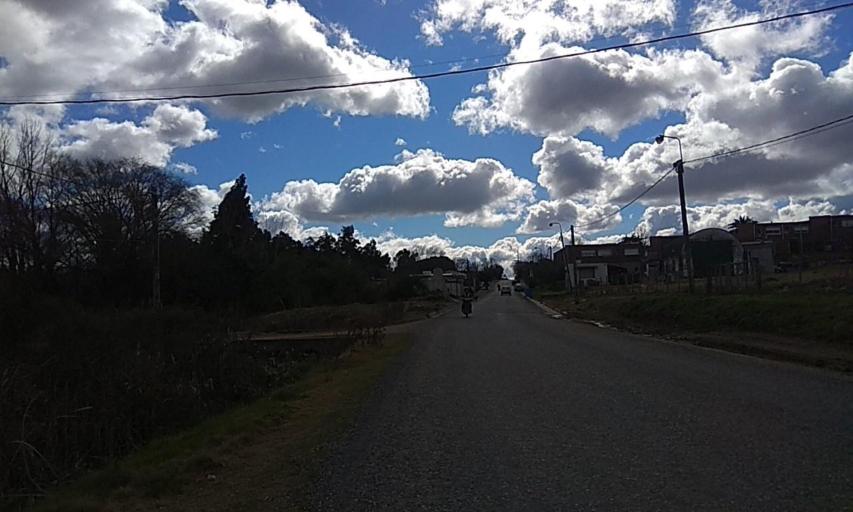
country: UY
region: Florida
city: Florida
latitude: -34.0888
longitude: -56.2261
